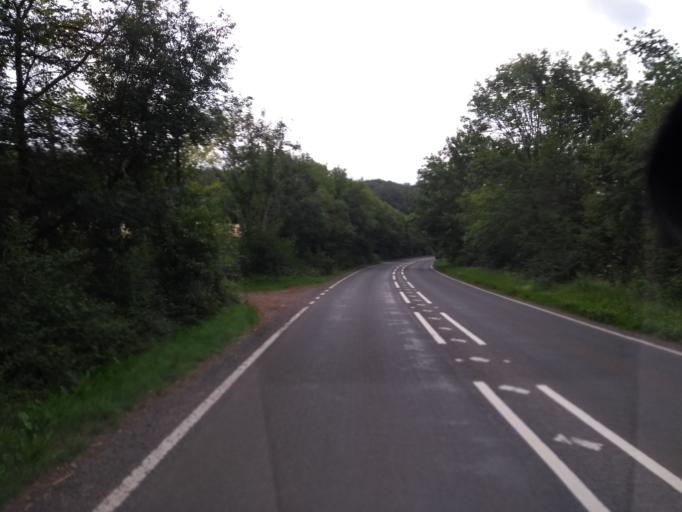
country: GB
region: England
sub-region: Somerset
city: Wiveliscombe
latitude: 51.0359
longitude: -3.2649
